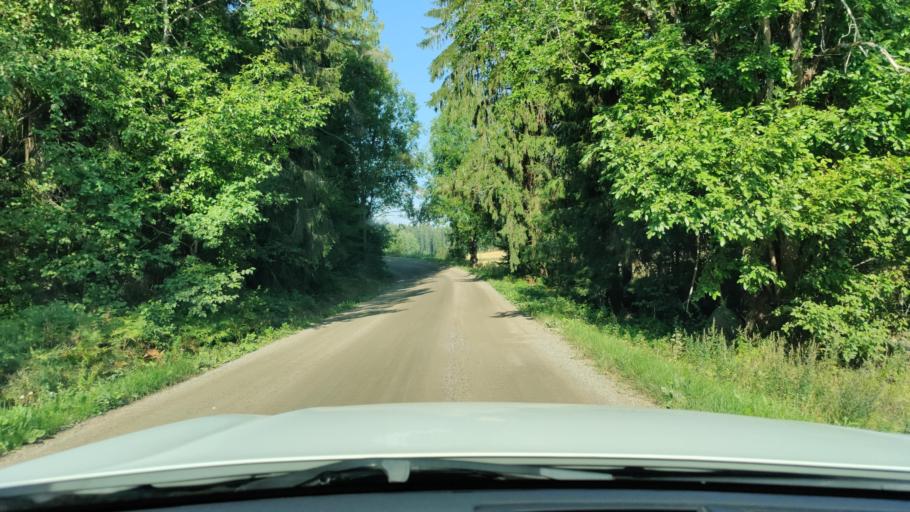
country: FI
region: Haeme
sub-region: Haemeenlinna
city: Tervakoski
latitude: 60.6738
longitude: 24.6096
